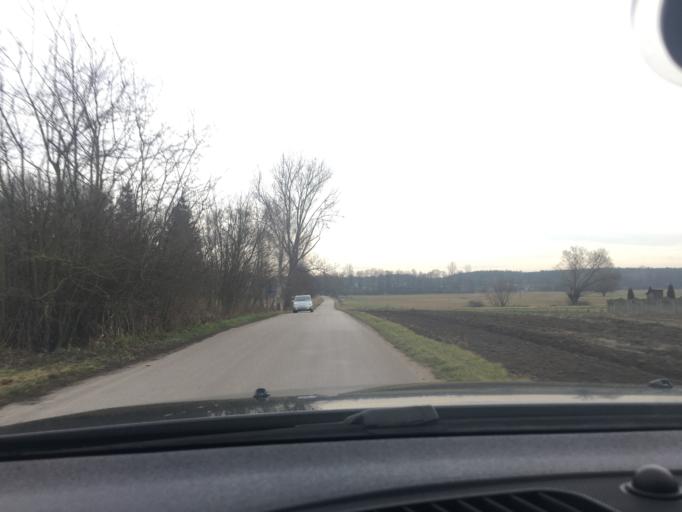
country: PL
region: Swietokrzyskie
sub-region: Powiat jedrzejowski
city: Imielno
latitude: 50.6363
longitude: 20.4136
